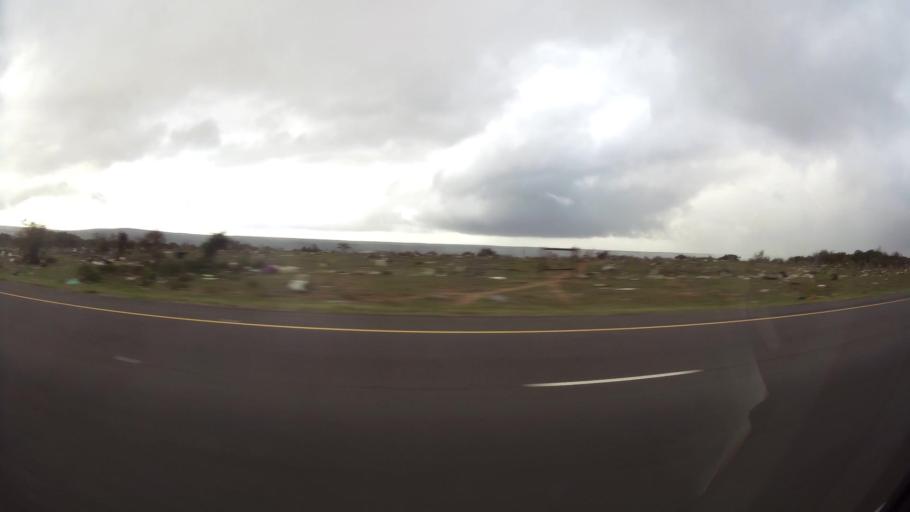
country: ZA
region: Eastern Cape
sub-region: Nelson Mandela Bay Metropolitan Municipality
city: Port Elizabeth
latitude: -33.8188
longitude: 25.5024
